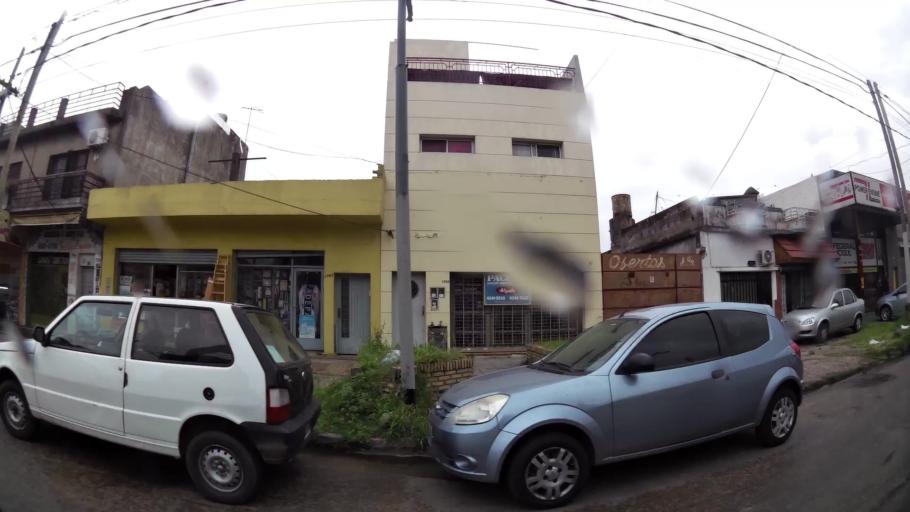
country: AR
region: Buenos Aires
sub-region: Partido de Lanus
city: Lanus
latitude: -34.6912
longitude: -58.4036
